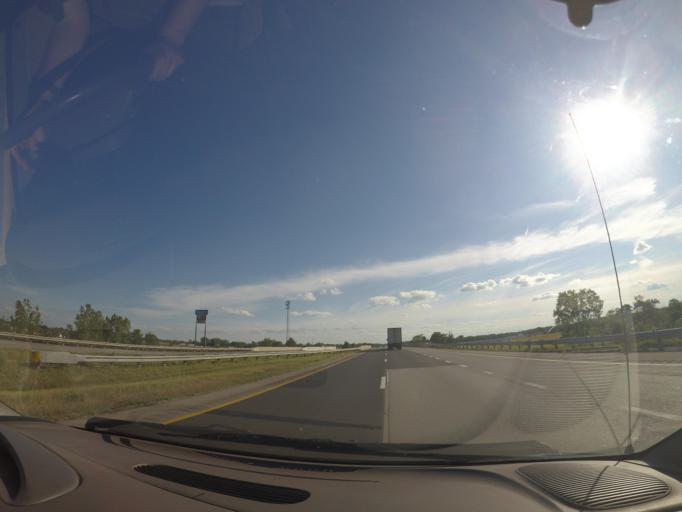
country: US
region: Ohio
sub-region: Henry County
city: Napoleon
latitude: 41.4070
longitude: -84.1342
